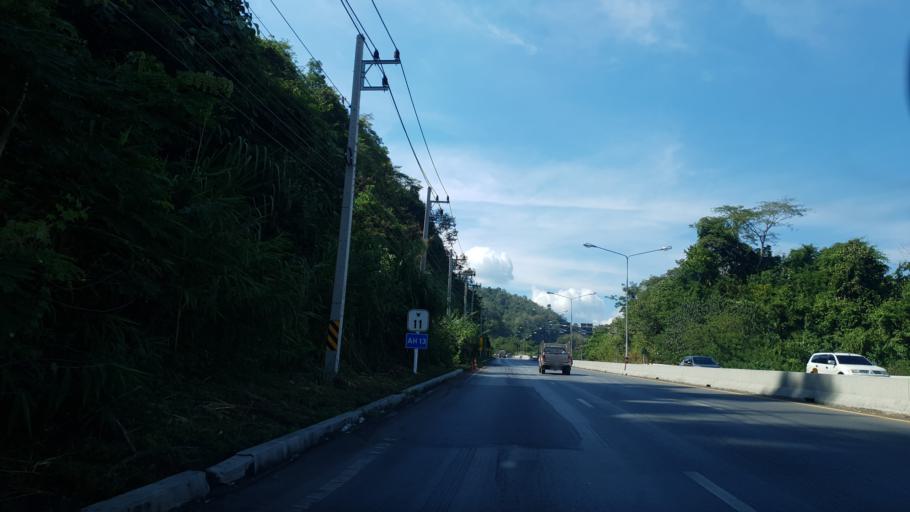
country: TH
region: Phrae
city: Den Chai
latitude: 17.8244
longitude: 100.0732
